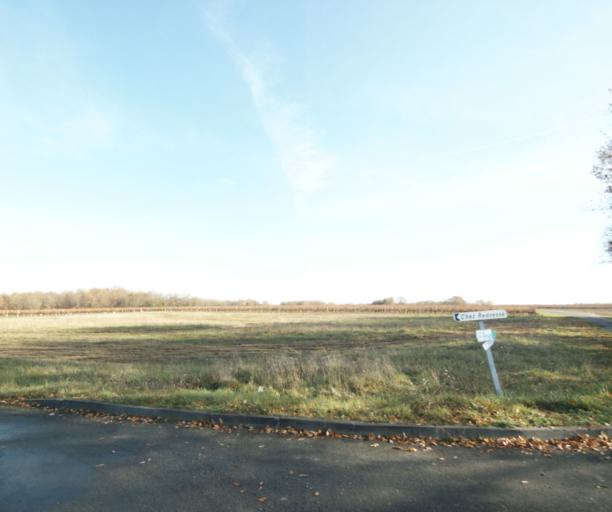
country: FR
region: Poitou-Charentes
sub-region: Departement de la Charente-Maritime
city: Cherac
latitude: 45.7517
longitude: -0.4921
